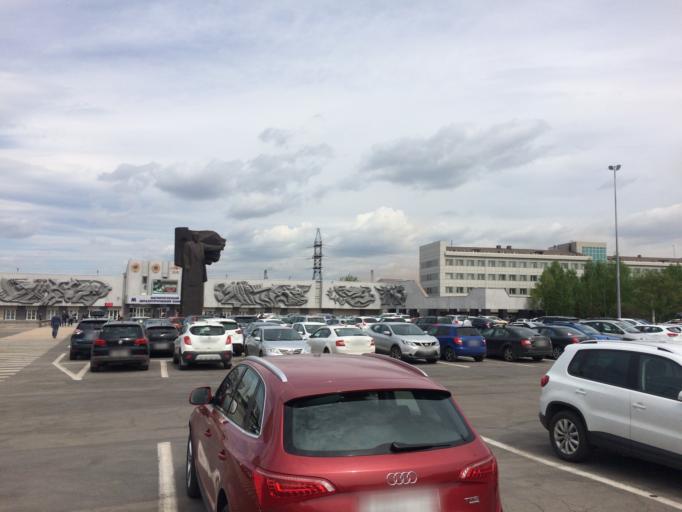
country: RU
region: Chelyabinsk
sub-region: Gorod Magnitogorsk
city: Magnitogorsk
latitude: 53.4146
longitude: 59.0548
